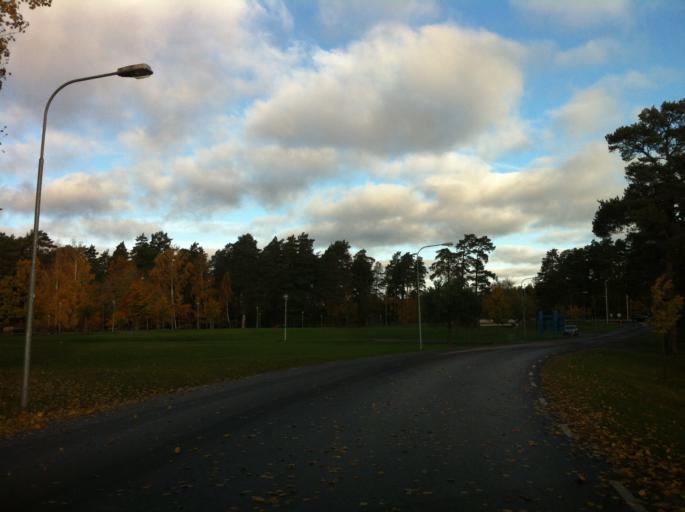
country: SE
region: OEstergoetland
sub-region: Linkopings Kommun
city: Linkoping
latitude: 58.4029
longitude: 15.5802
